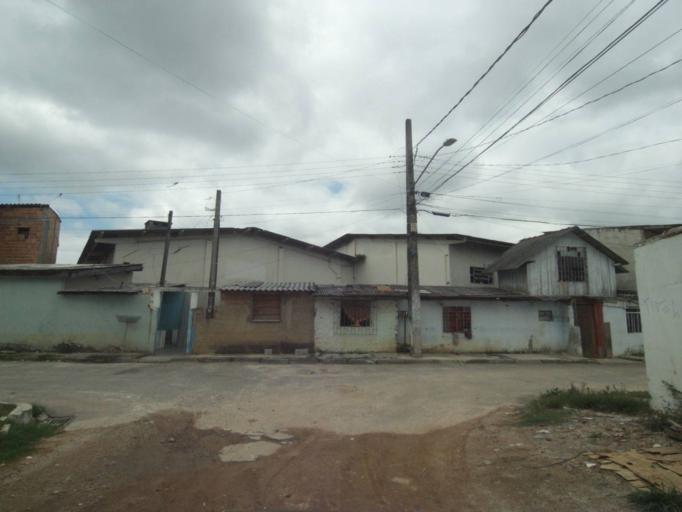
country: BR
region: Parana
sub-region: Pinhais
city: Pinhais
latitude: -25.4474
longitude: -49.2011
